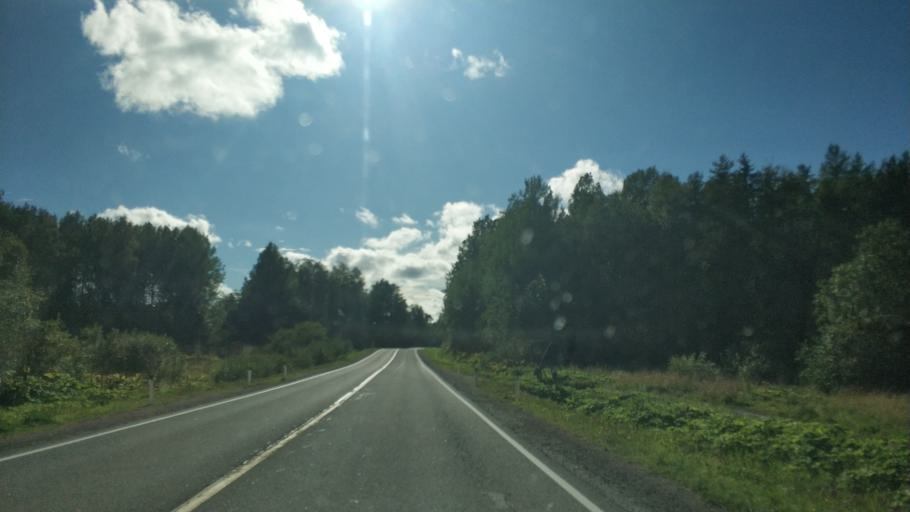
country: RU
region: Republic of Karelia
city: Khelyulya
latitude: 61.6507
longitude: 30.6019
